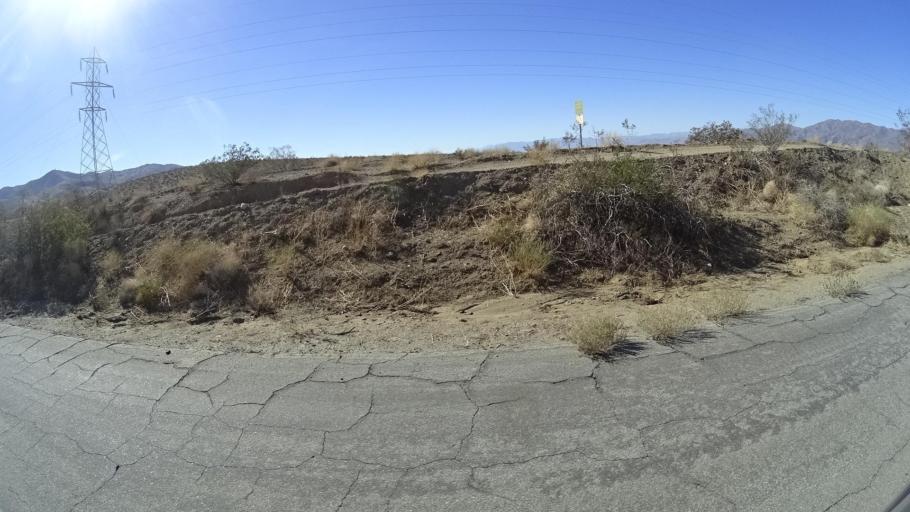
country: US
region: California
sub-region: Kern County
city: Ridgecrest
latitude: 35.3951
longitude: -117.6717
